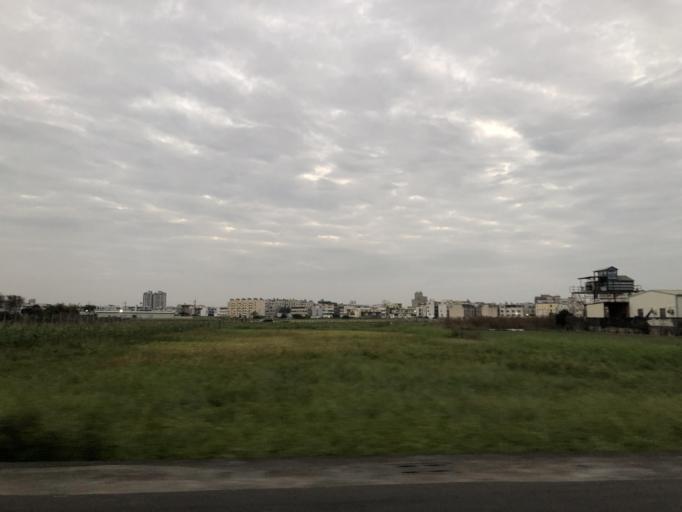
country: TW
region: Taiwan
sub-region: Tainan
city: Tainan
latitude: 23.0209
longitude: 120.2691
